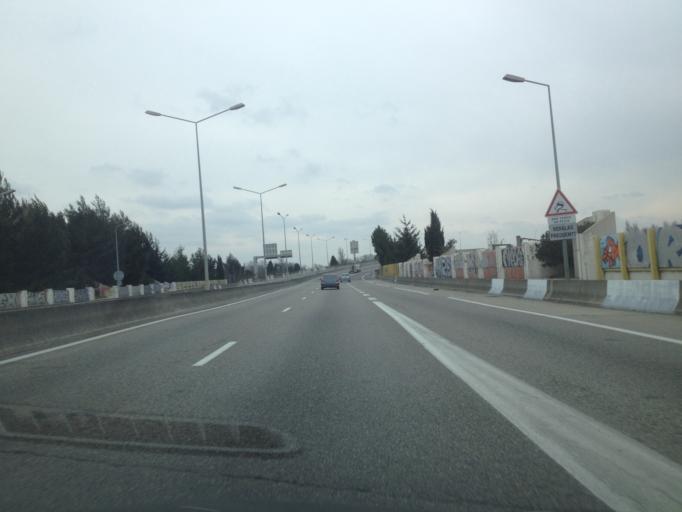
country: FR
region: Provence-Alpes-Cote d'Azur
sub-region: Departement du Vaucluse
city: Le Pontet
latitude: 43.9539
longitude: 4.8401
